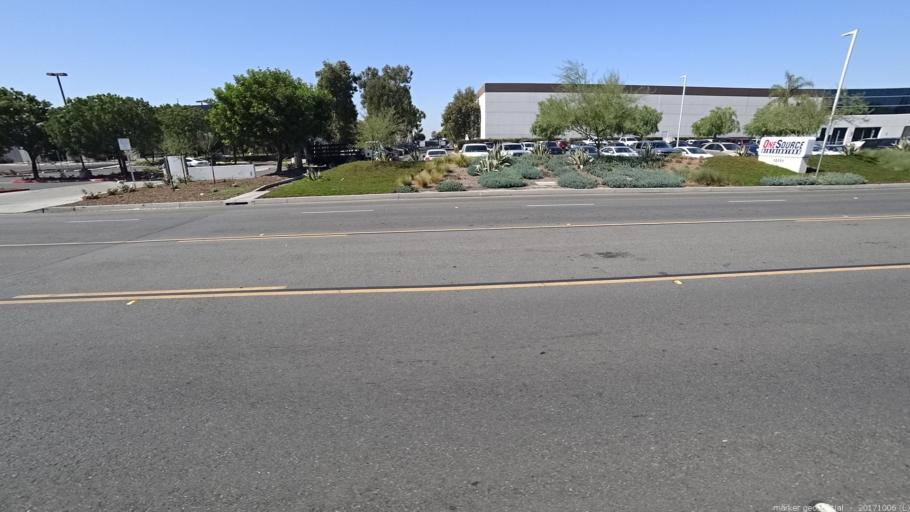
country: US
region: California
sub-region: Orange County
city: Stanton
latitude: 33.7860
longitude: -118.0014
